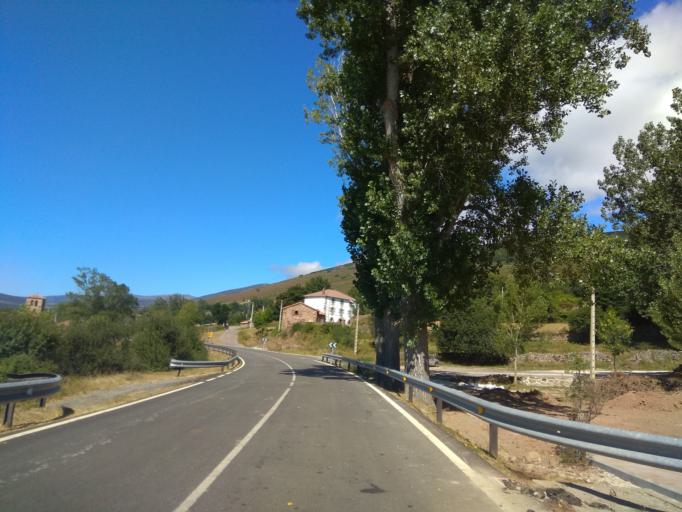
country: ES
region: Cantabria
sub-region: Provincia de Cantabria
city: Villaescusa
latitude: 42.9391
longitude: -4.1835
